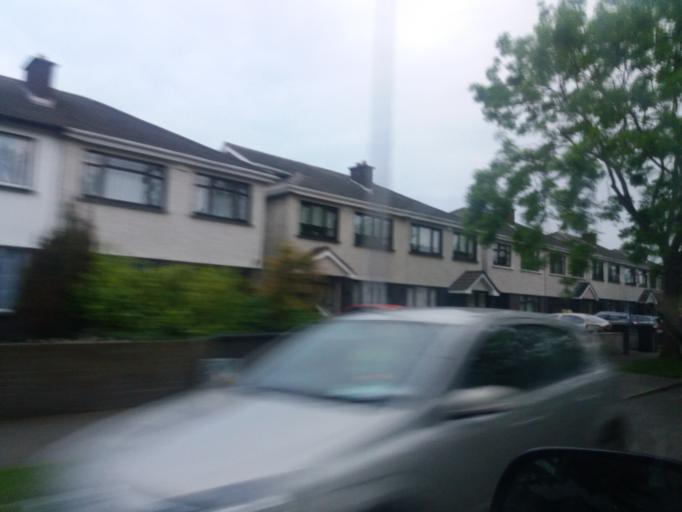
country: IE
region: Leinster
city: Raheny
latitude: 53.3932
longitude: -6.1847
